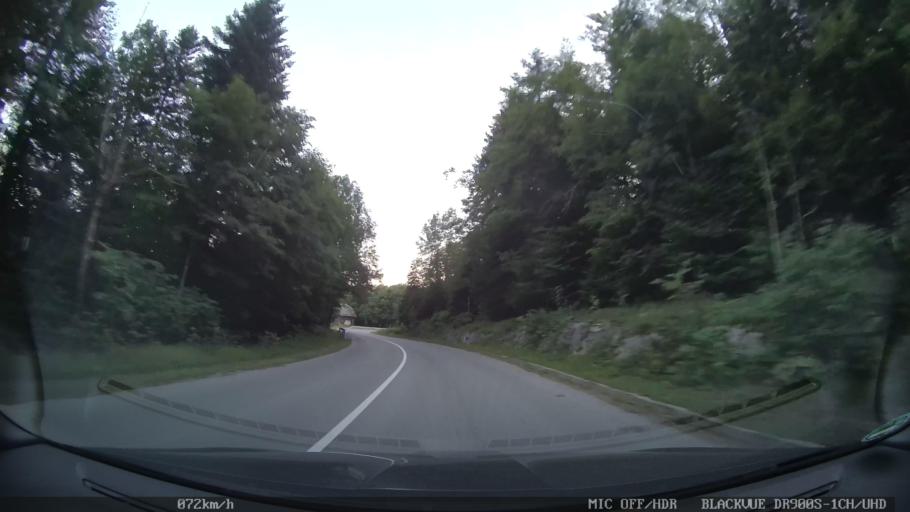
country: HR
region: Primorsko-Goranska
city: Novi Vinodolski
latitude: 45.1698
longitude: 14.9647
